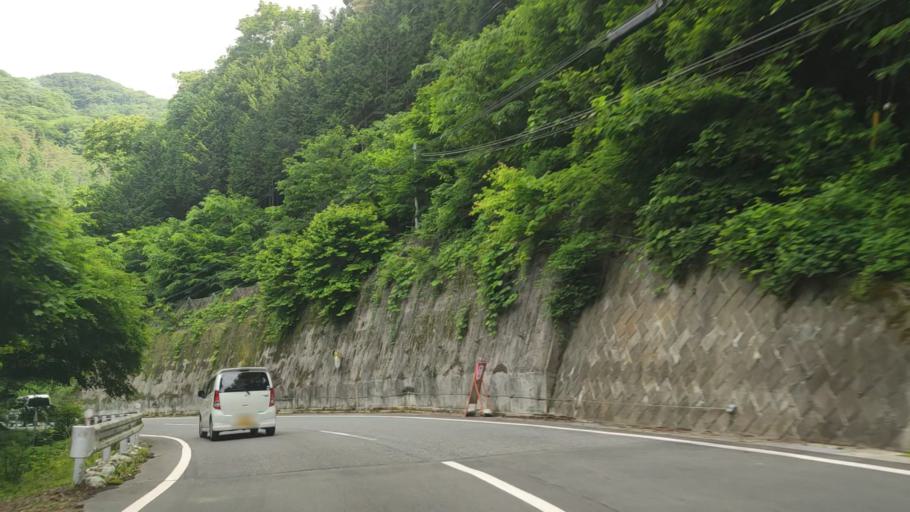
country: JP
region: Gunma
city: Tomioka
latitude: 36.1009
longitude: 138.7172
